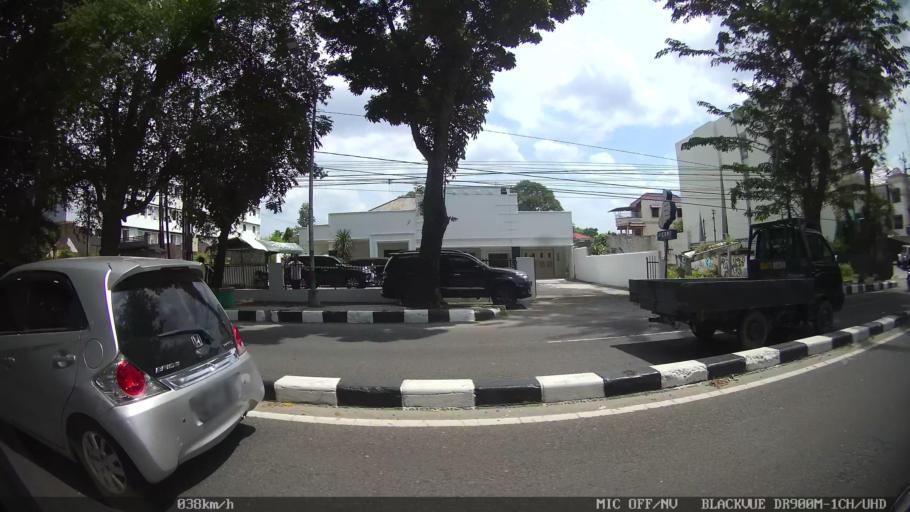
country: ID
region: North Sumatra
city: Medan
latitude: 3.5711
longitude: 98.6671
